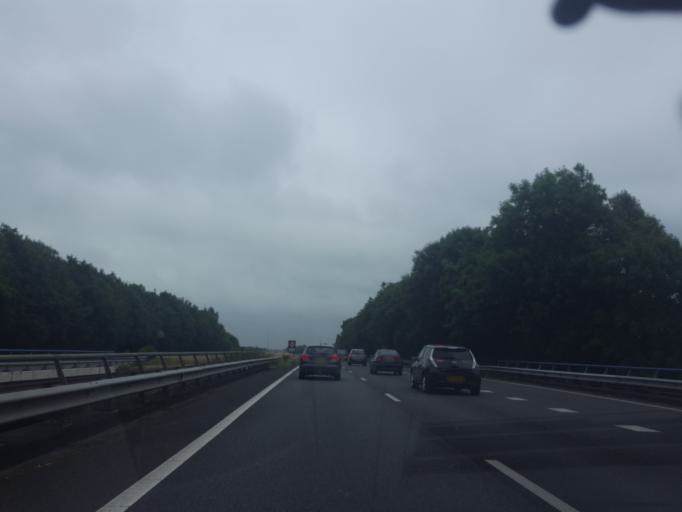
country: NL
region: Friesland
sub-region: Gemeente Lemsterland
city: Lemmer
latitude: 52.8477
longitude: 5.7222
